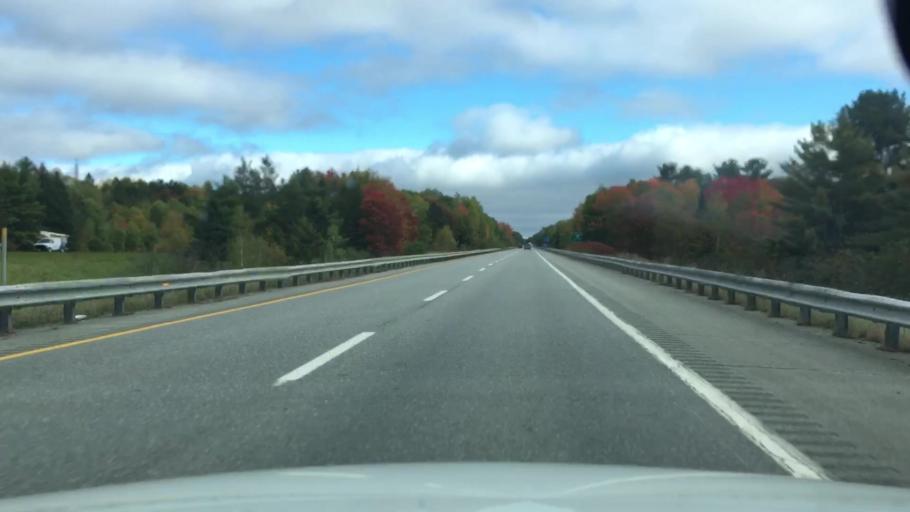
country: US
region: Maine
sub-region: Penobscot County
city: Carmel
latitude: 44.7687
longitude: -68.9989
